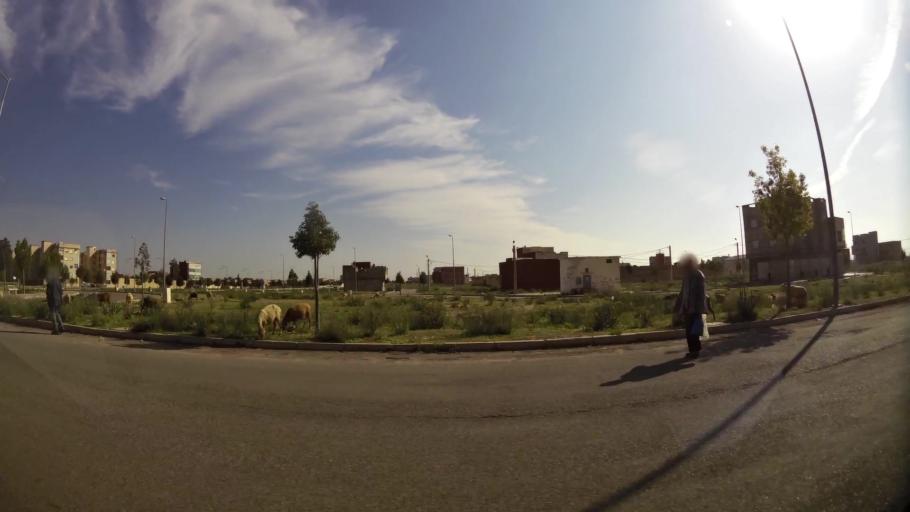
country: MA
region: Oriental
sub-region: Oujda-Angad
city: Oujda
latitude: 34.7173
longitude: -1.8840
